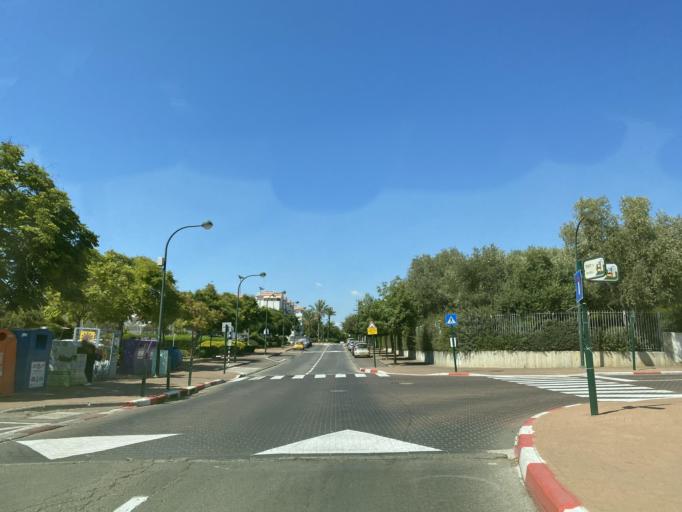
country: IL
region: Central District
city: Ra'anana
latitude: 32.1865
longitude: 34.8867
